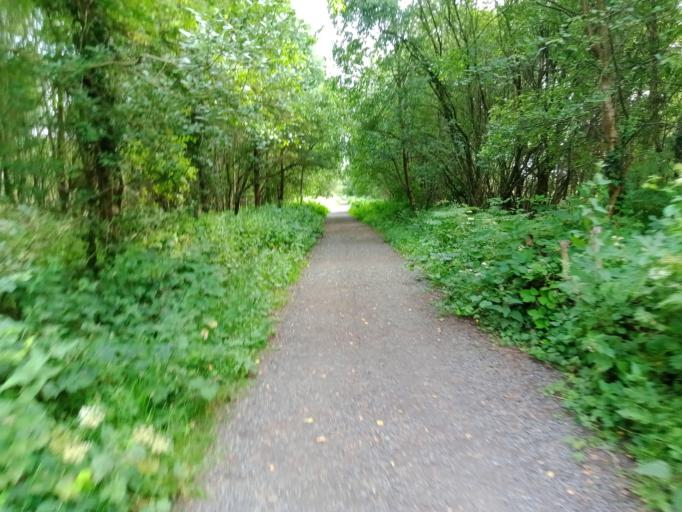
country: IE
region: Leinster
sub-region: Laois
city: Abbeyleix
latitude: 52.8986
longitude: -7.3502
